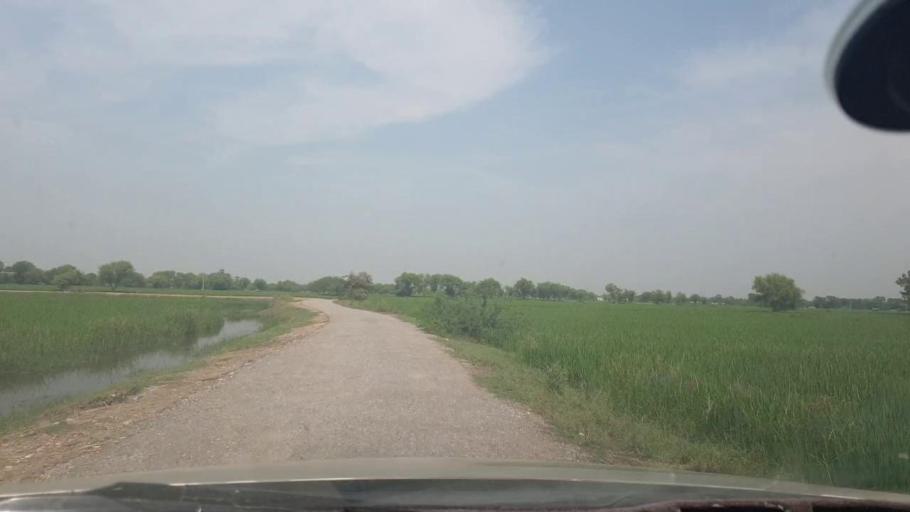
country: PK
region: Sindh
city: Jacobabad
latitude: 28.2421
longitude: 68.4277
